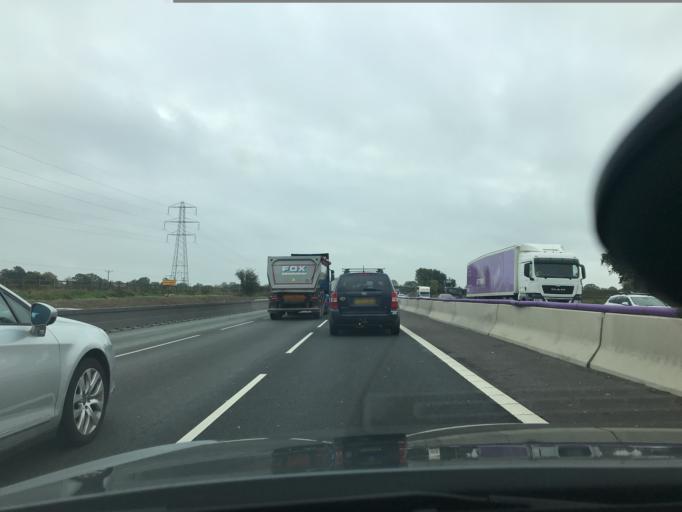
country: GB
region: England
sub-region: Cheshire East
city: Knutsford
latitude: 53.2781
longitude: -2.3968
